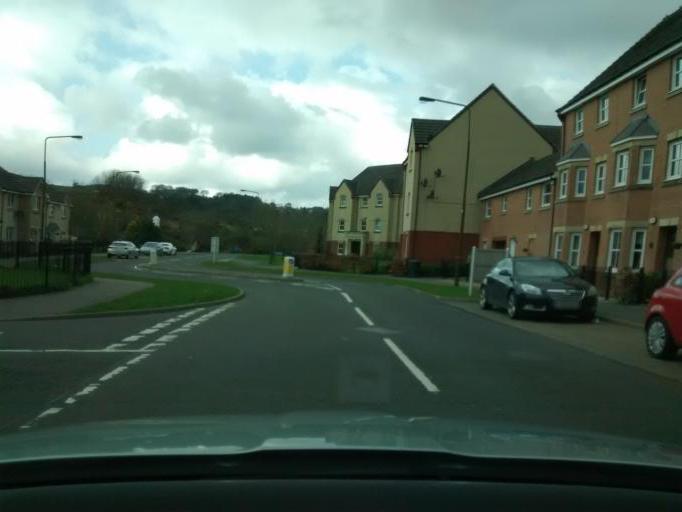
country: GB
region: Scotland
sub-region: West Lothian
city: Bathgate
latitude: 55.8907
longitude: -3.6233
